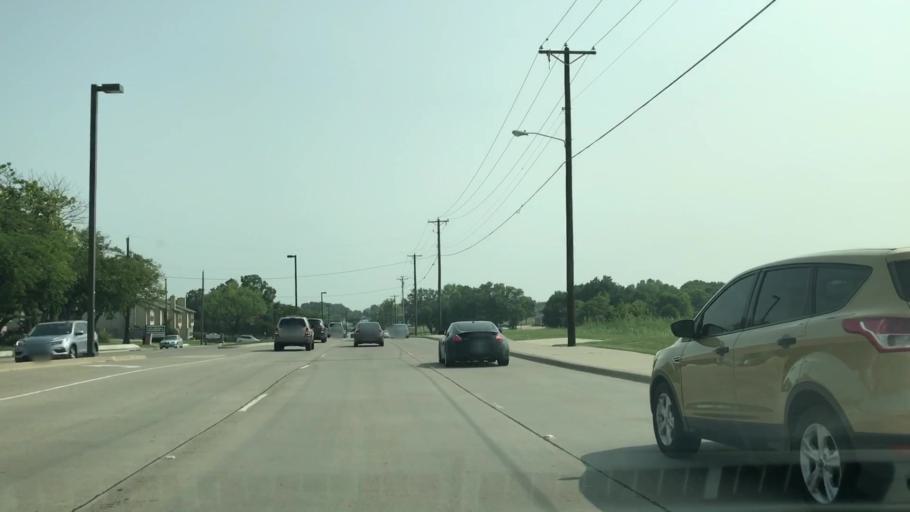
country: US
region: Texas
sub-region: Dallas County
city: Rowlett
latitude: 32.8991
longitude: -96.5696
